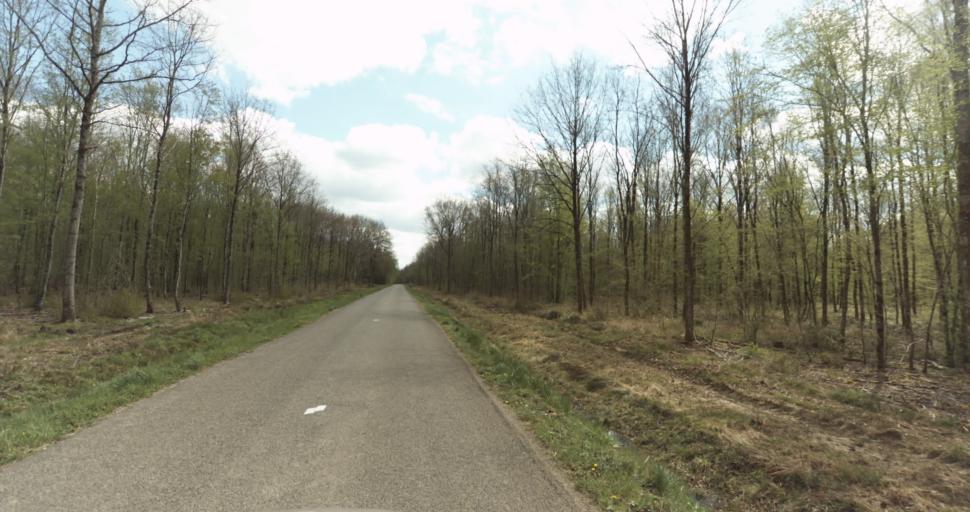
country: FR
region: Bourgogne
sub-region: Departement de la Cote-d'Or
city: Auxonne
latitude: 47.1669
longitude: 5.4435
